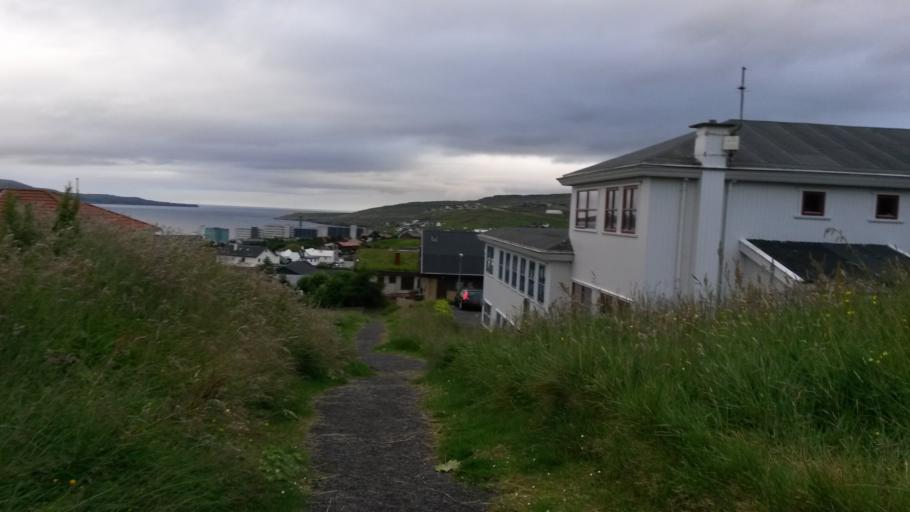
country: FO
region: Streymoy
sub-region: Torshavn
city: Torshavn
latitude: 62.0092
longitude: -6.7924
